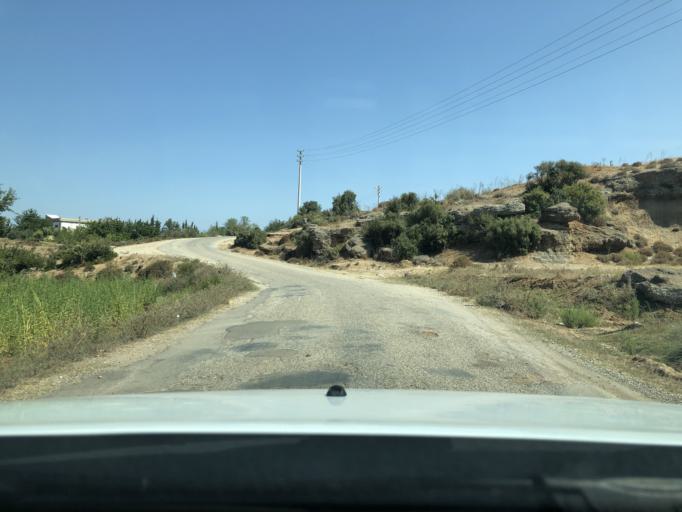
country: TR
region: Antalya
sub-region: Manavgat
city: Manavgat
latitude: 36.8035
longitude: 31.4709
